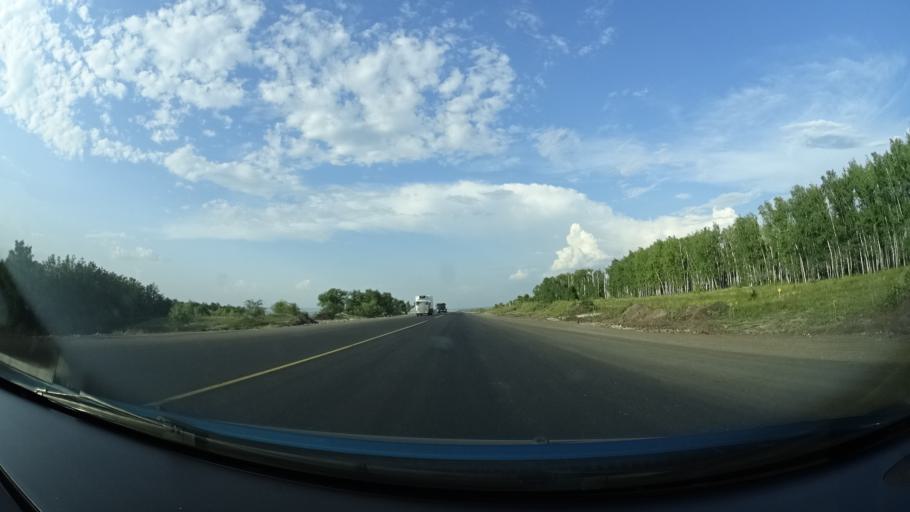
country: RU
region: Samara
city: Sukhodol
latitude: 53.7417
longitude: 50.8558
